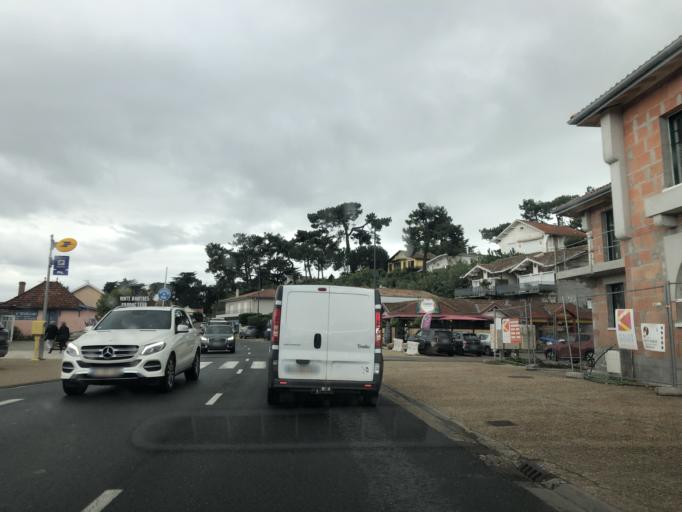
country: FR
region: Aquitaine
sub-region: Departement de la Gironde
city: Arcachon
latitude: 44.7005
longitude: -1.2299
